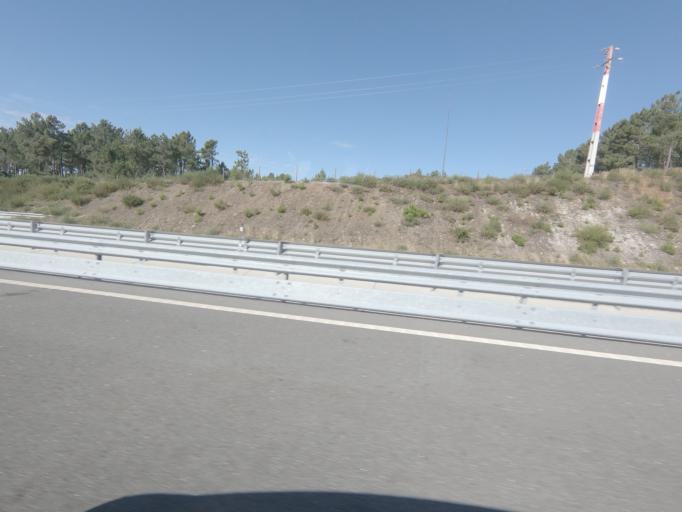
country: PT
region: Vila Real
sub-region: Santa Marta de Penaguiao
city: Santa Marta de Penaguiao
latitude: 41.2722
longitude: -7.8175
